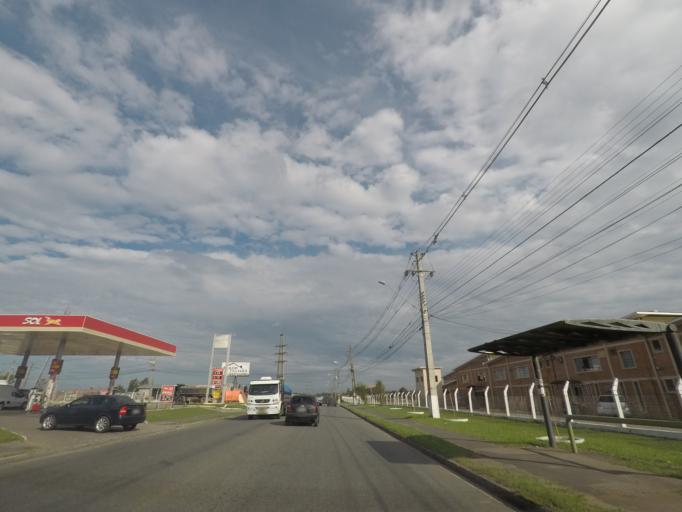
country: BR
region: Parana
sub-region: Sao Jose Dos Pinhais
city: Sao Jose dos Pinhais
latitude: -25.5475
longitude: -49.2934
